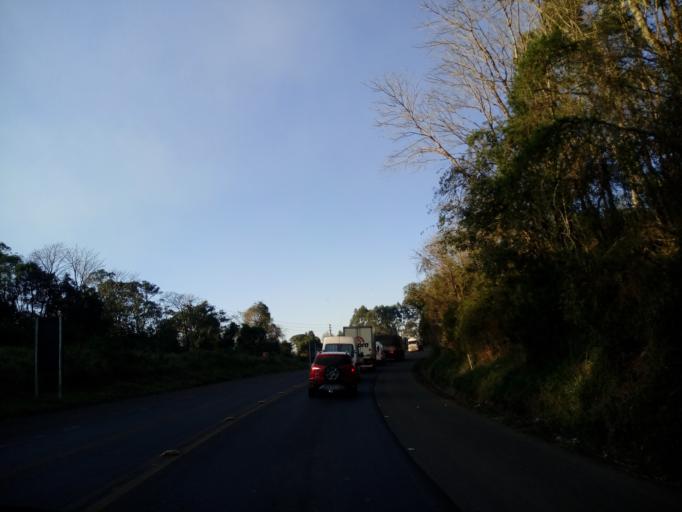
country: BR
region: Santa Catarina
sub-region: Chapeco
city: Chapeco
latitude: -27.2297
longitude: -52.6847
